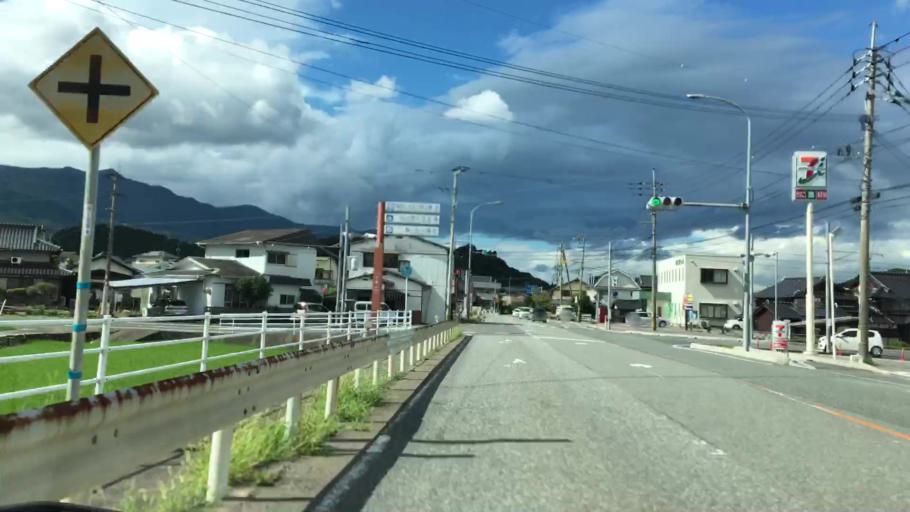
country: JP
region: Saga Prefecture
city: Imaricho-ko
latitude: 33.1925
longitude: 129.8512
